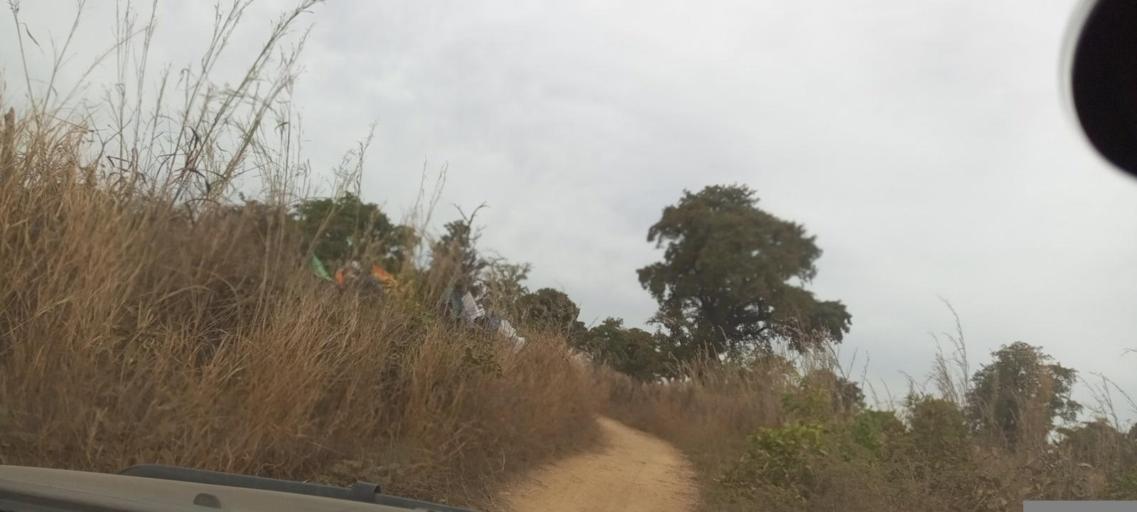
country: ML
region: Koulikoro
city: Kati
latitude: 12.7454
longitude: -8.3554
